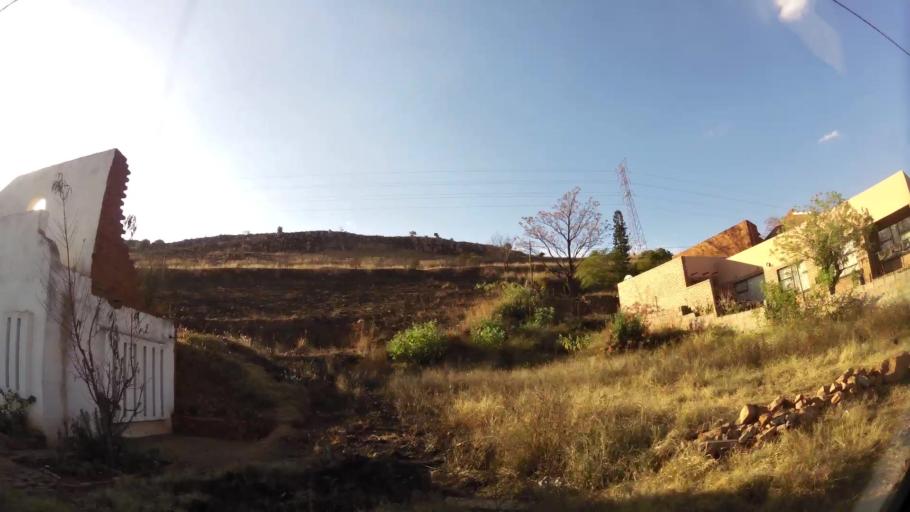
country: ZA
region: Gauteng
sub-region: City of Tshwane Metropolitan Municipality
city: Cullinan
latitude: -25.7030
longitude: 28.3812
